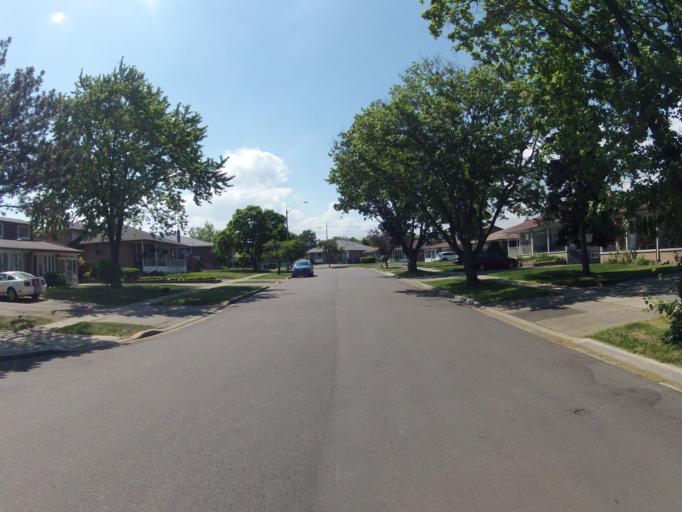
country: CA
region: Ontario
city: Mississauga
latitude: 43.5150
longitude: -79.6498
